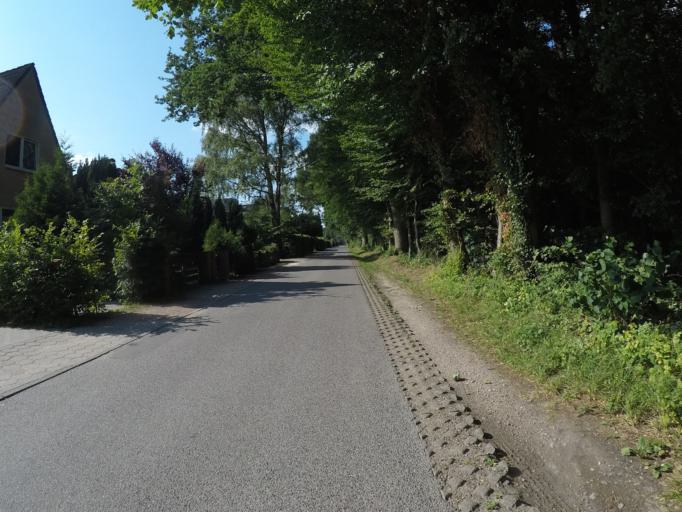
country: DE
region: Hamburg
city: Sasel
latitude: 53.6339
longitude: 10.1298
